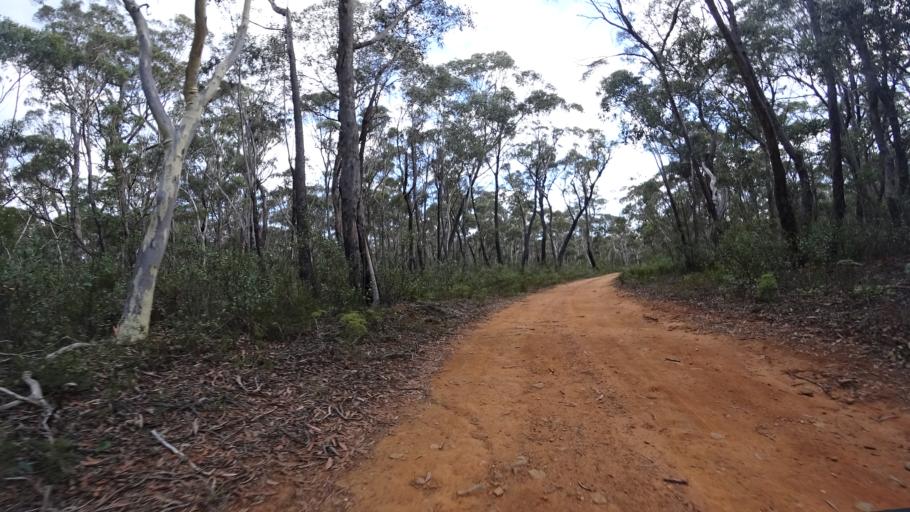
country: AU
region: New South Wales
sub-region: Lithgow
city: Lithgow
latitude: -33.3426
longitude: 150.2673
